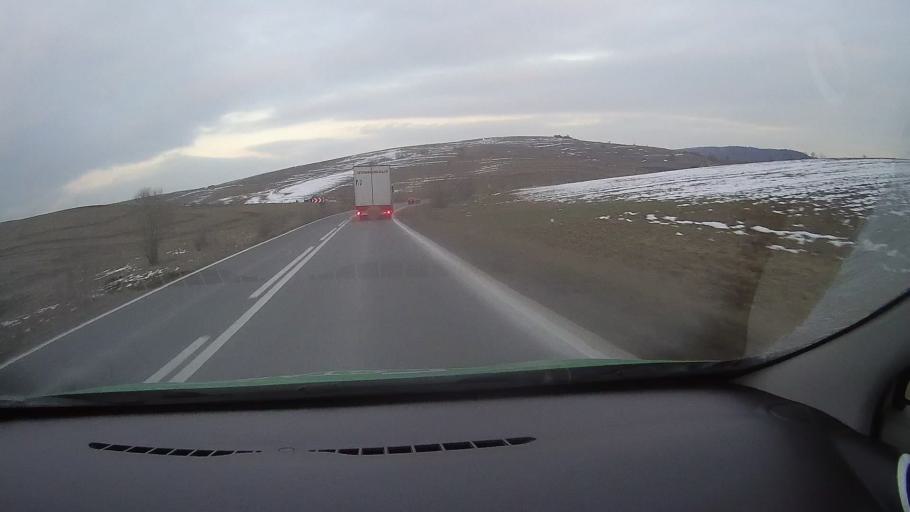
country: RO
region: Harghita
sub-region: Comuna Lupeni
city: Lupeni
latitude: 46.3507
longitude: 25.2608
